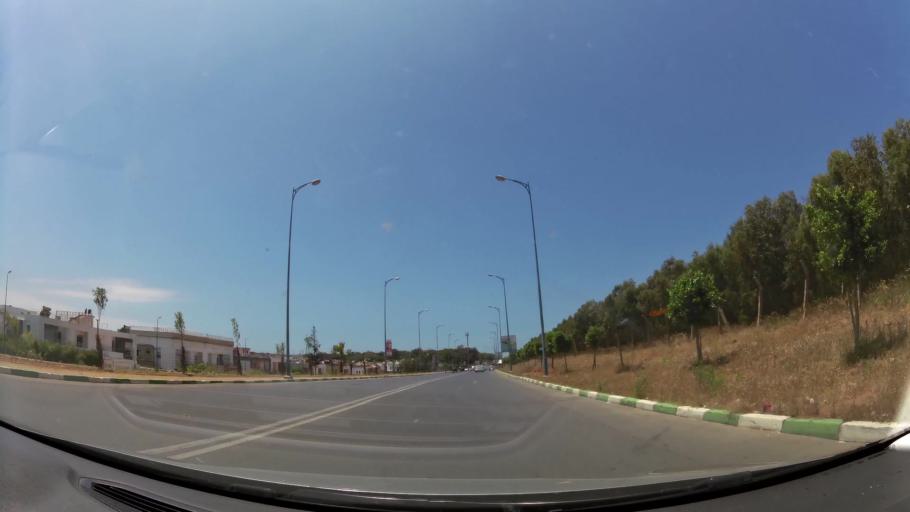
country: MA
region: Gharb-Chrarda-Beni Hssen
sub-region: Kenitra Province
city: Kenitra
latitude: 34.2712
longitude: -6.6371
